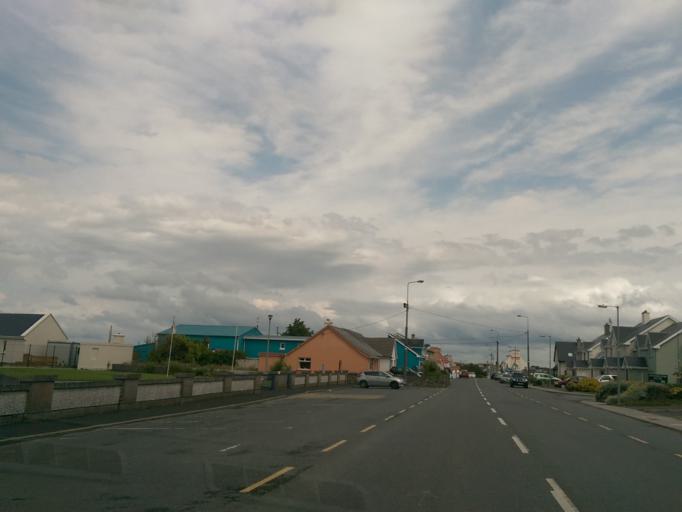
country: IE
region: Munster
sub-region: An Clar
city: Kilrush
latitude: 52.7303
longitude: -9.5300
